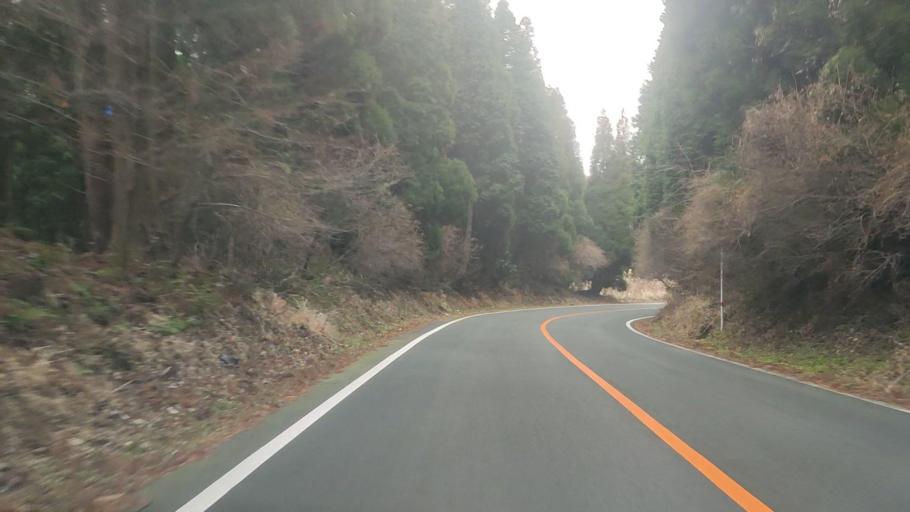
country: JP
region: Kumamoto
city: Aso
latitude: 32.9079
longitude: 131.1441
